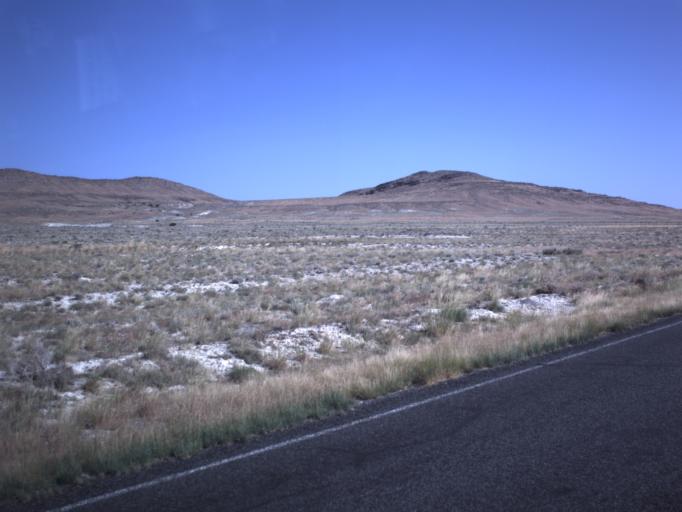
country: US
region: Utah
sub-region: Beaver County
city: Milford
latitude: 38.8610
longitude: -112.8387
